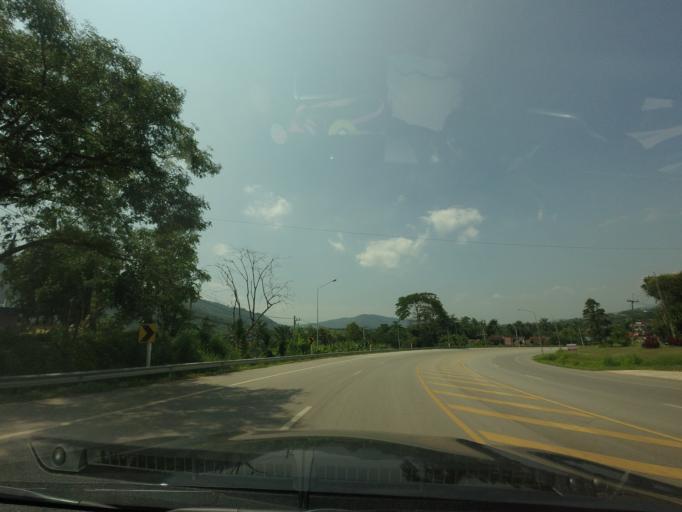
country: TH
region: Loei
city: Phu Ruea
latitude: 17.4565
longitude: 101.3780
